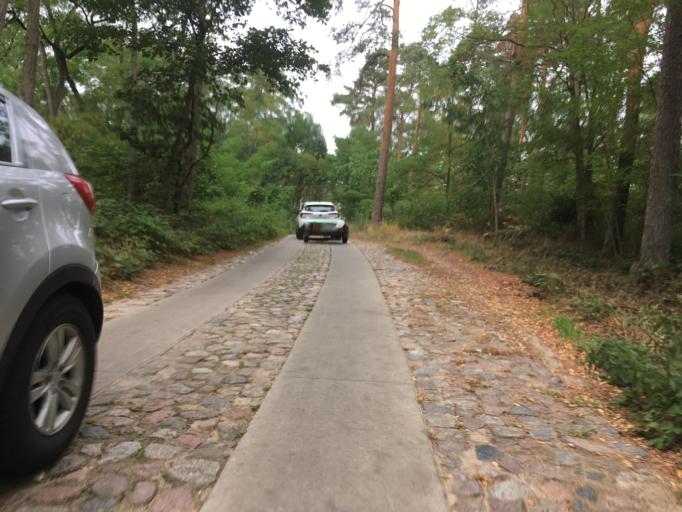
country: DE
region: Brandenburg
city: Gerswalde
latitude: 53.1934
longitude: 13.8323
